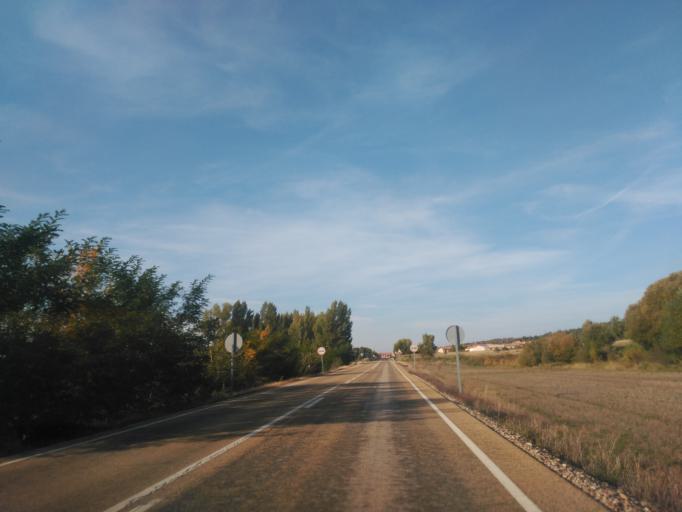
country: ES
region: Castille and Leon
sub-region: Provincia de Soria
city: Valdemaluque
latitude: 41.6686
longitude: -3.0480
